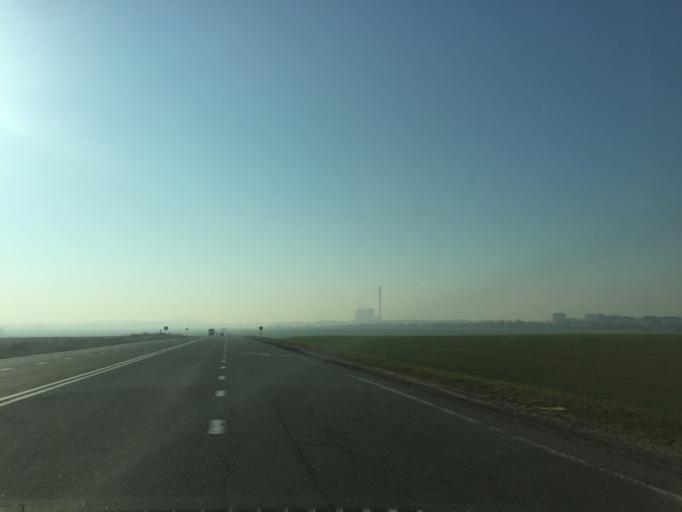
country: BY
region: Gomel
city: Kastsyukowka
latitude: 52.4770
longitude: 30.8217
